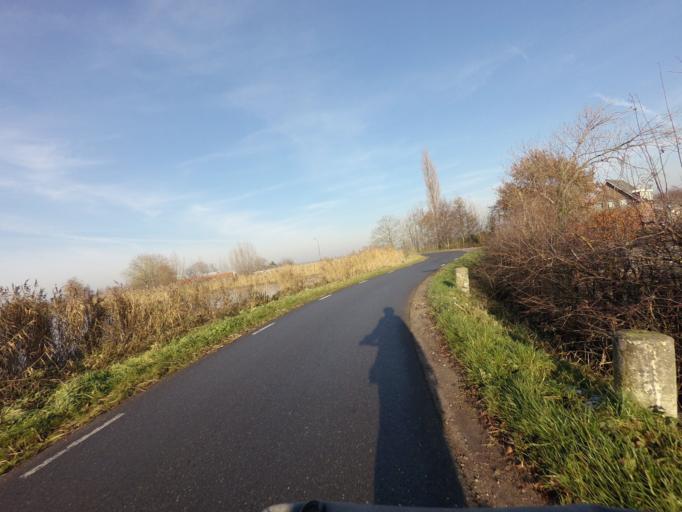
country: NL
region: Utrecht
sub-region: Gemeente De Ronde Venen
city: Mijdrecht
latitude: 52.1902
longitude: 4.8287
